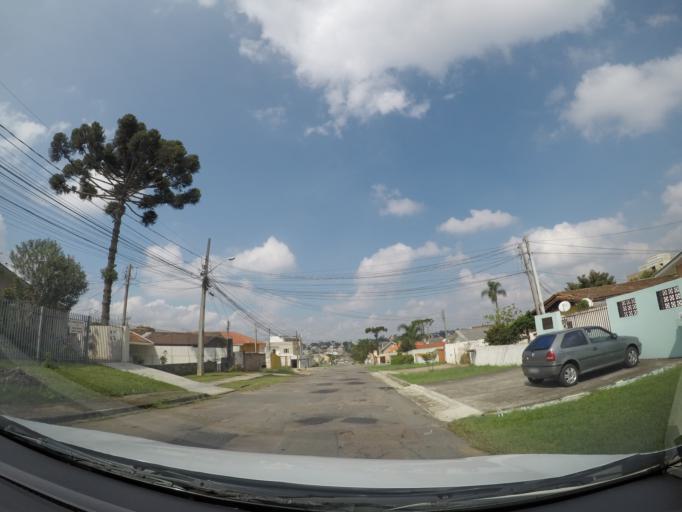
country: BR
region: Parana
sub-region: Sao Jose Dos Pinhais
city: Sao Jose dos Pinhais
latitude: -25.4967
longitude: -49.2619
